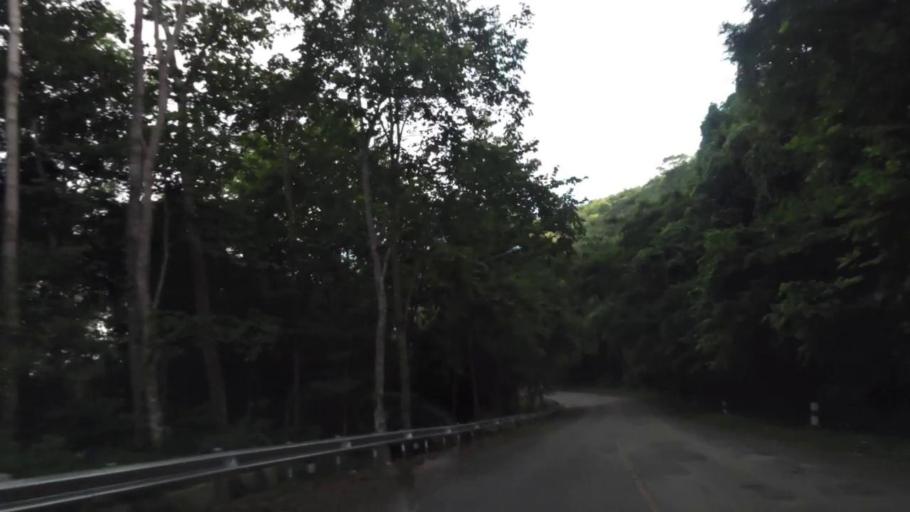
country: TH
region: Chiang Rai
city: Khun Tan
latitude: 19.8654
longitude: 100.4429
